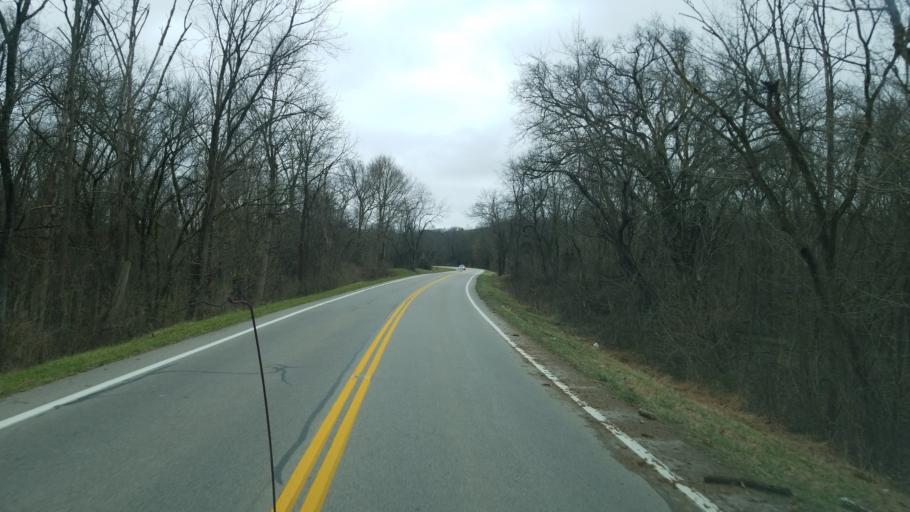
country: US
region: Ohio
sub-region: Clermont County
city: New Richmond
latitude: 38.8174
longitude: -84.2154
